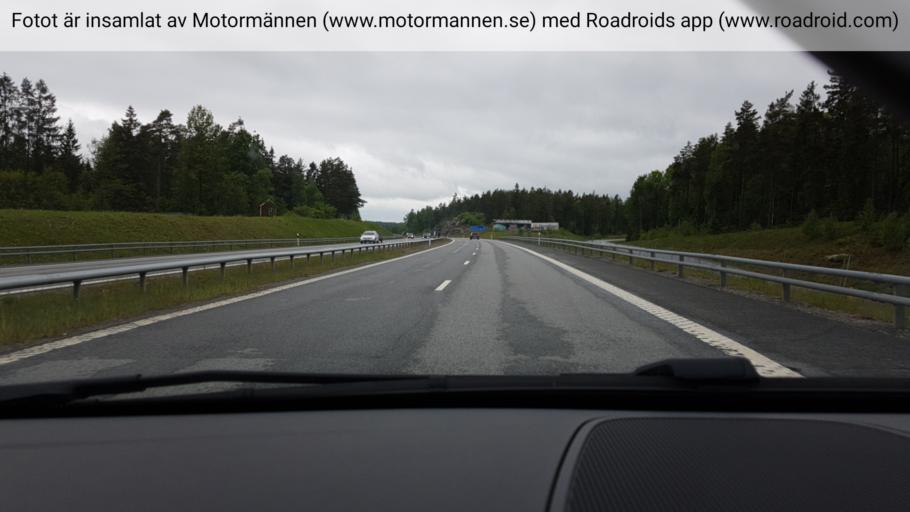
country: SE
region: Stockholm
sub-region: Haninge Kommun
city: Jordbro
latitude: 59.0757
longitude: 18.0723
